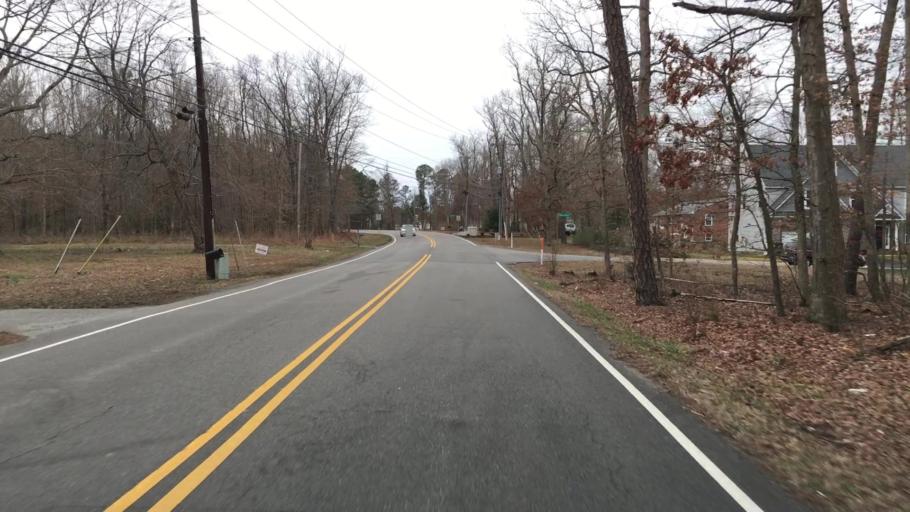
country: US
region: Virginia
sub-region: Henrico County
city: Glen Allen
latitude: 37.6712
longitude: -77.5564
